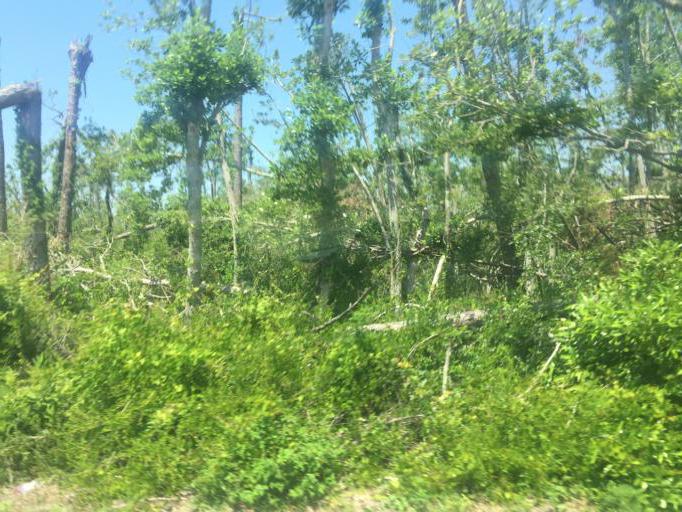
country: US
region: Florida
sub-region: Bay County
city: Lynn Haven
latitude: 30.2125
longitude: -85.6623
